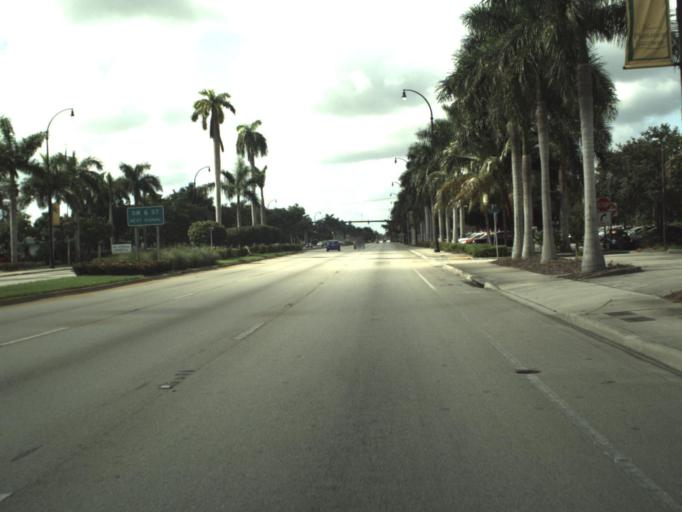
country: US
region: Florida
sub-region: Broward County
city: Melrose Park
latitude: 26.1158
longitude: -80.2019
